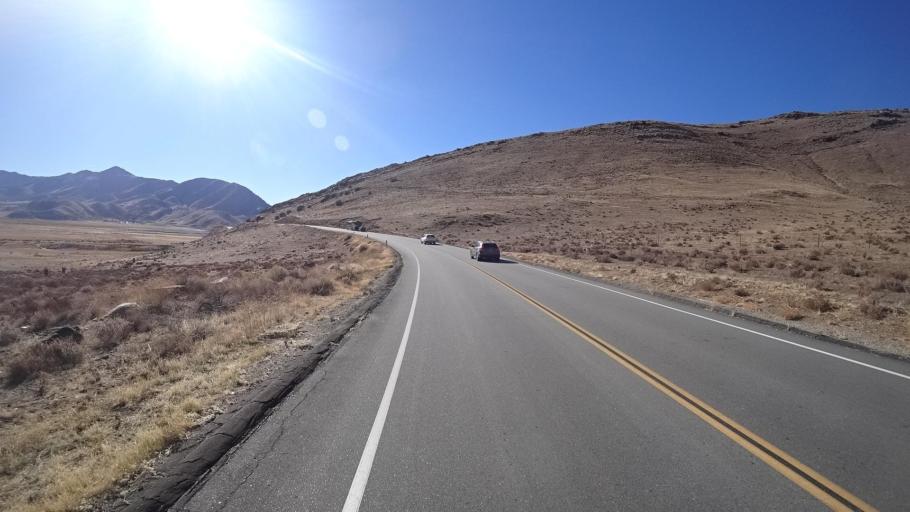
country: US
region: California
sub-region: Kern County
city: Wofford Heights
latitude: 35.6801
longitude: -118.4122
